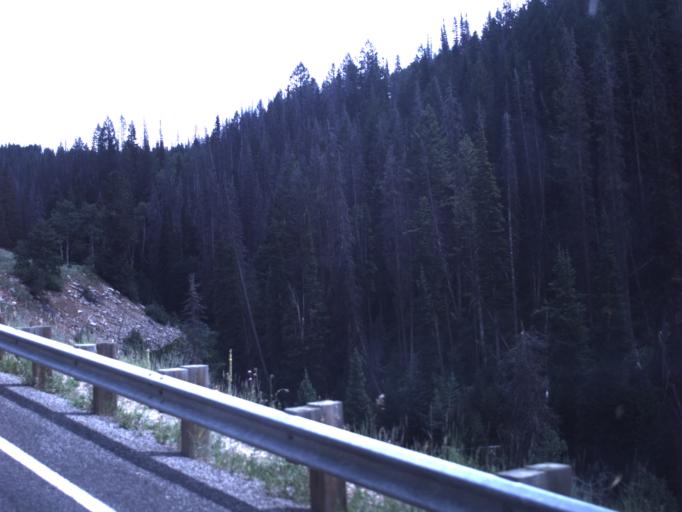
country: US
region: Utah
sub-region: Summit County
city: Francis
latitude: 40.5162
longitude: -111.0535
